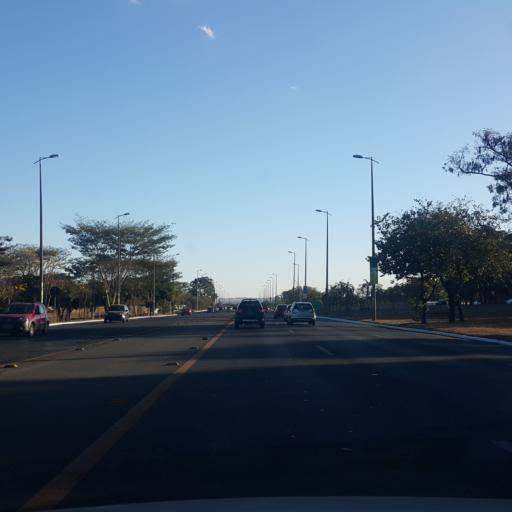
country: BR
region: Federal District
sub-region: Brasilia
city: Brasilia
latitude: -15.8328
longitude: -47.9226
